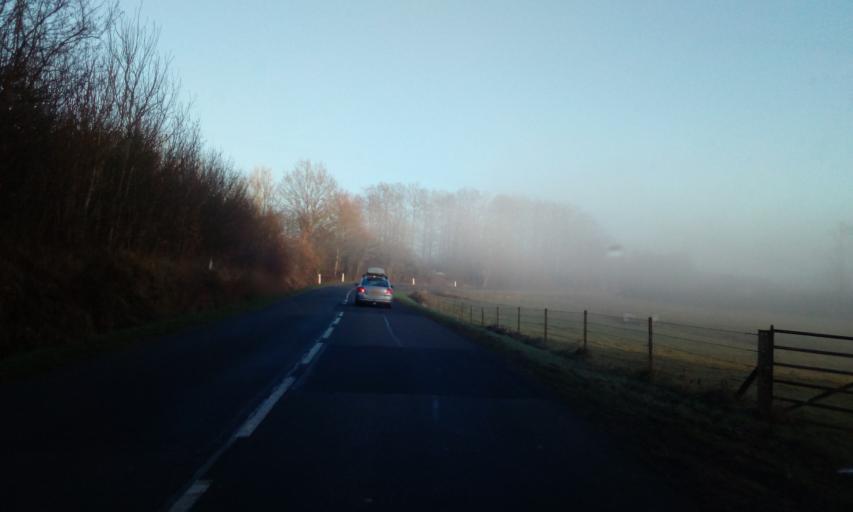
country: FR
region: Champagne-Ardenne
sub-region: Departement des Ardennes
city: Renwez
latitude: 49.8125
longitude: 4.5766
